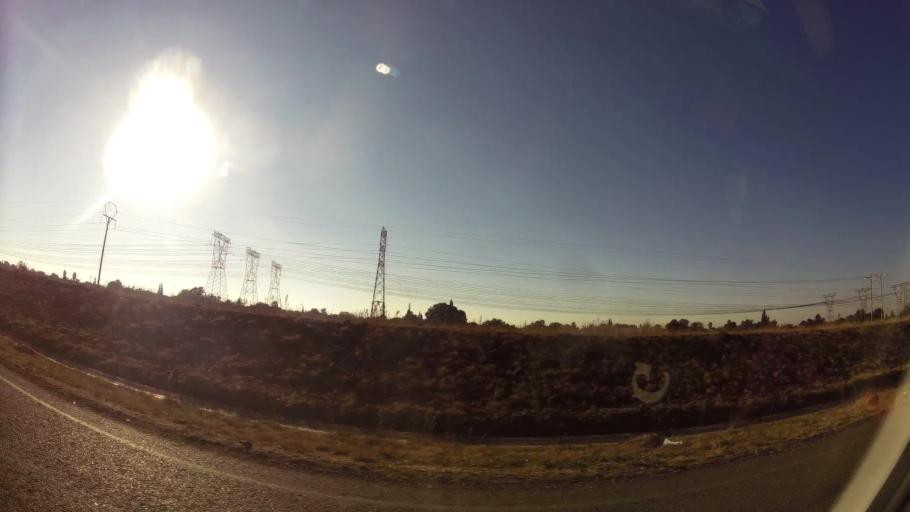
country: ZA
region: Gauteng
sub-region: Ekurhuleni Metropolitan Municipality
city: Germiston
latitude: -26.3213
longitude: 28.1128
